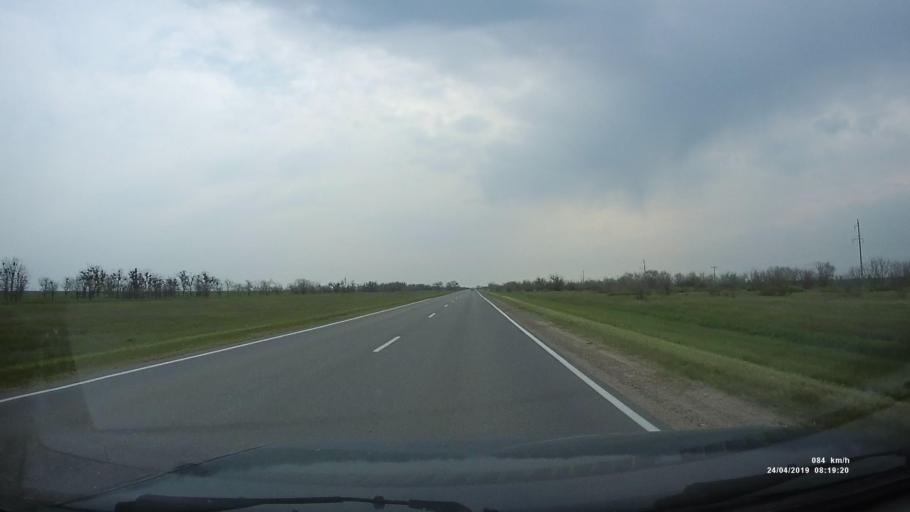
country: RU
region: Kalmykiya
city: Priyutnoye
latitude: 46.1038
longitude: 43.6634
